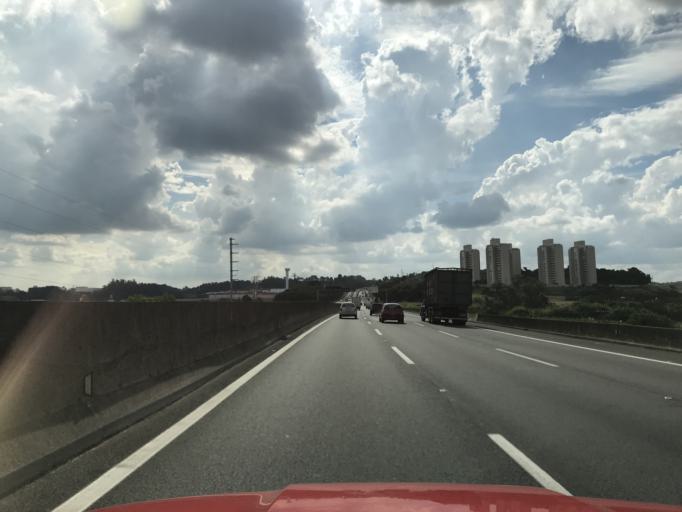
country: BR
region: Sao Paulo
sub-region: Jundiai
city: Jundiai
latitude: -23.1658
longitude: -46.9286
